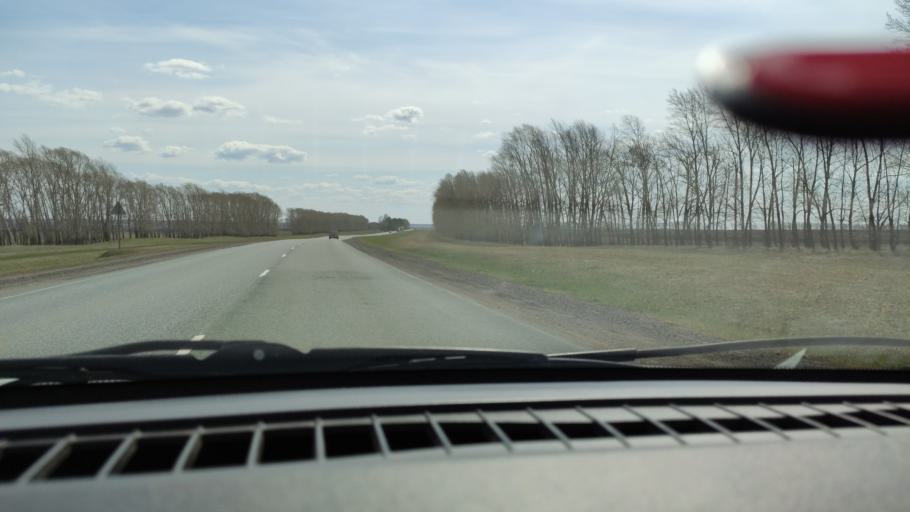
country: RU
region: Bashkortostan
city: Kushnarenkovo
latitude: 55.1858
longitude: 55.1241
